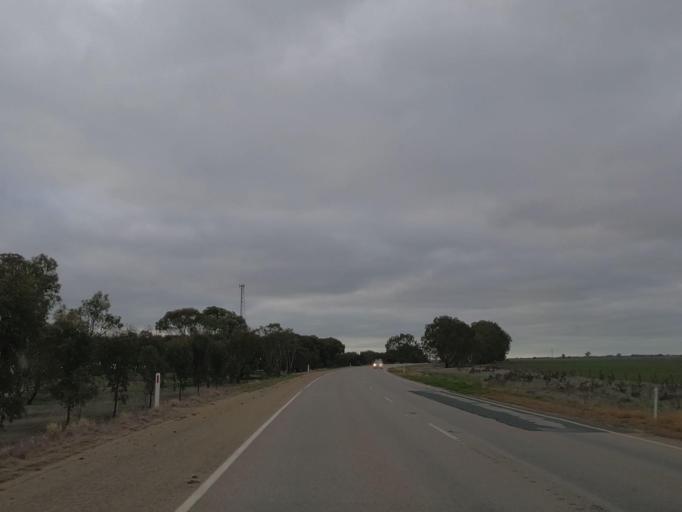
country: AU
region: Victoria
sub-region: Swan Hill
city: Swan Hill
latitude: -35.9256
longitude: 143.9365
